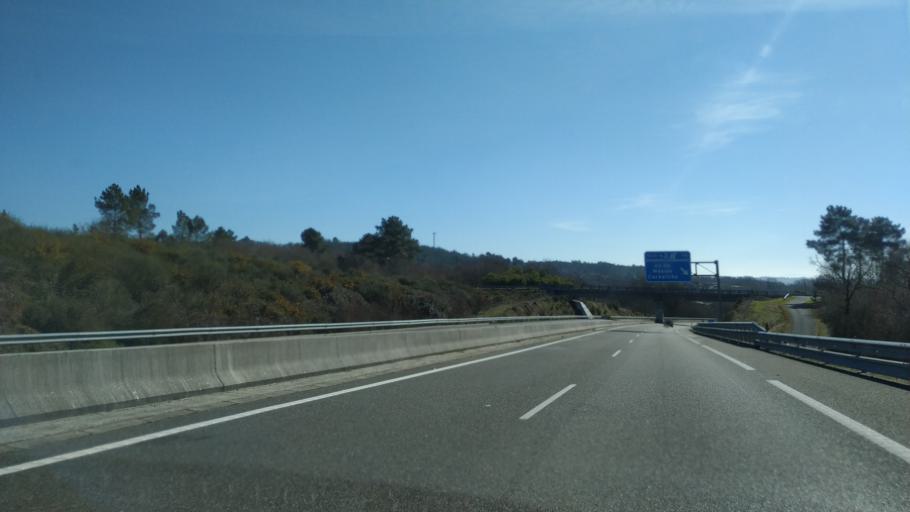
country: ES
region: Galicia
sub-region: Provincia de Ourense
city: Maside
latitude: 42.4143
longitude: -8.0150
